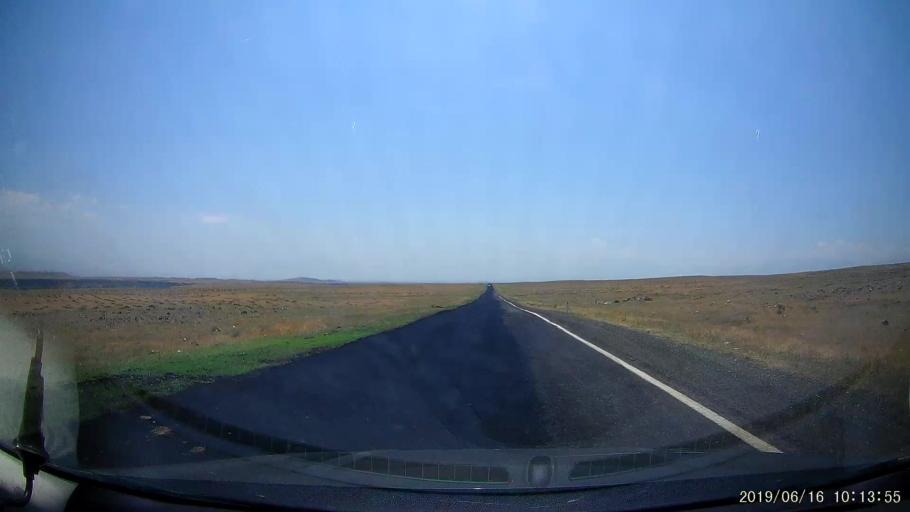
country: TR
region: Igdir
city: Tuzluca
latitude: 40.1894
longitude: 43.6521
